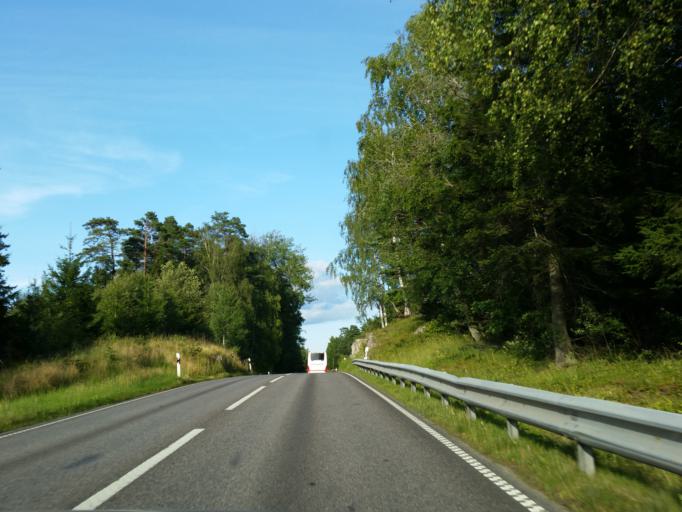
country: SE
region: Stockholm
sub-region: Sodertalje Kommun
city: Molnbo
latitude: 59.0381
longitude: 17.3785
